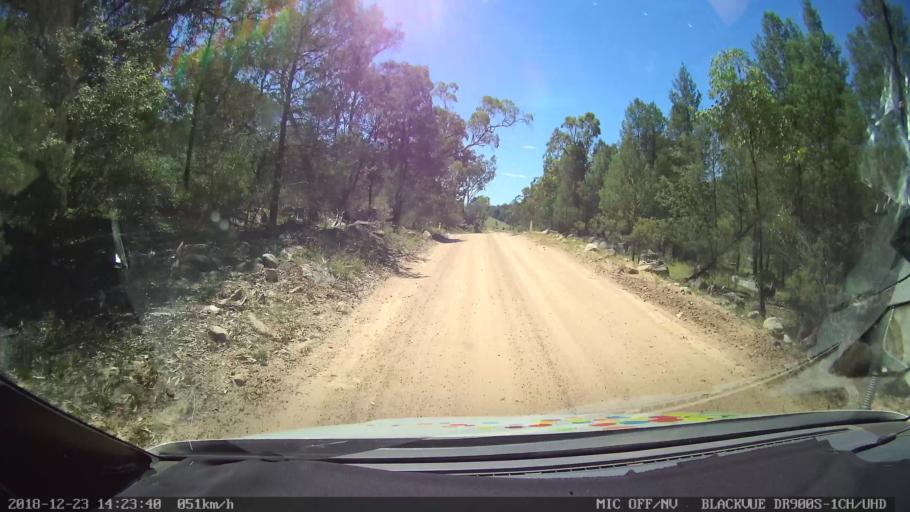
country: AU
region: New South Wales
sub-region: Tamworth Municipality
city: Manilla
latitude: -30.6355
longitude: 150.9658
